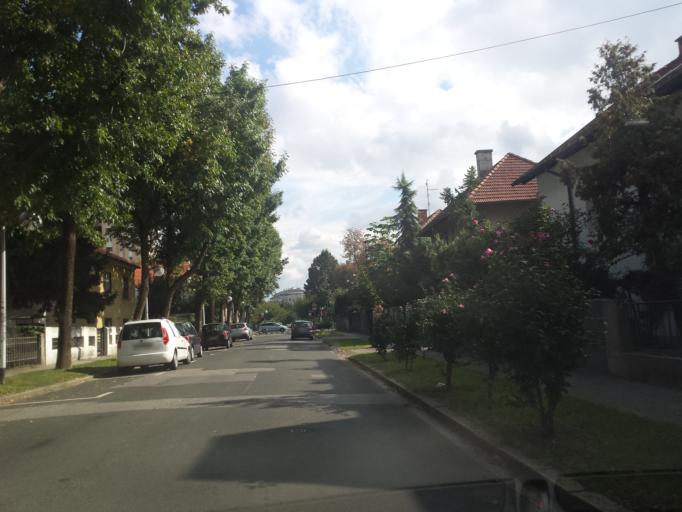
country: HR
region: Grad Zagreb
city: Zagreb
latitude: 45.8141
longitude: 16.0039
